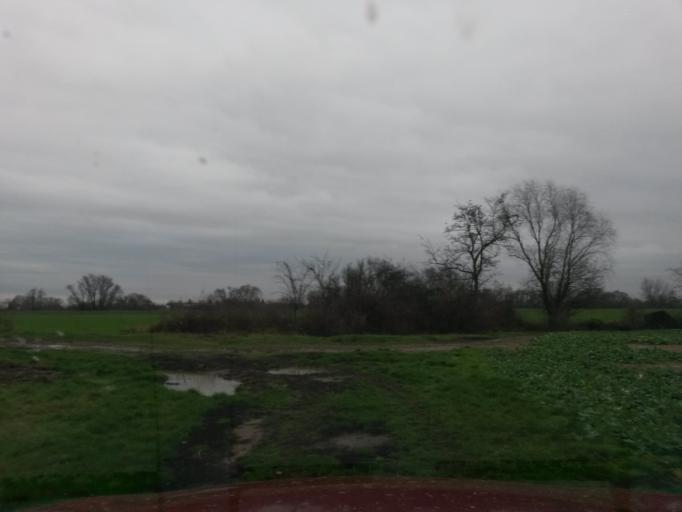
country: SK
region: Kosicky
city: Sobrance
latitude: 48.6362
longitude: 22.0883
